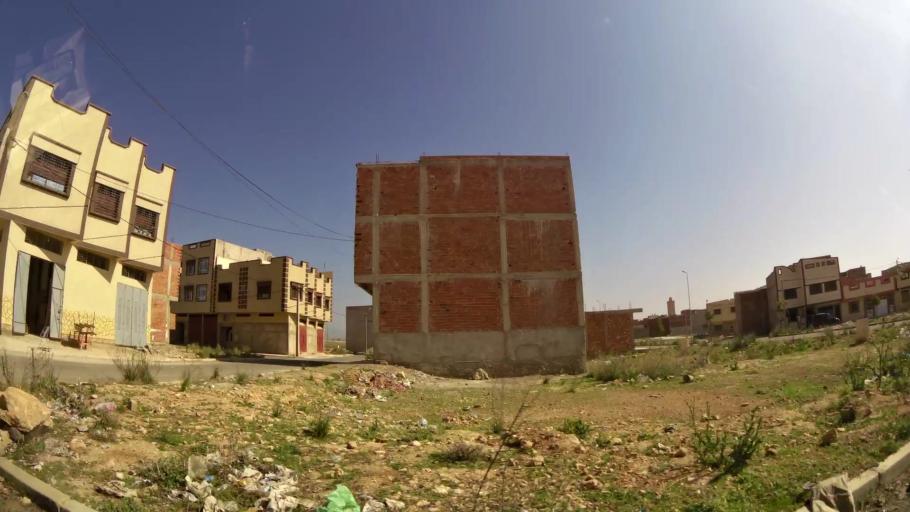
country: MA
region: Oriental
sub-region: Oujda-Angad
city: Oujda
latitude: 34.6969
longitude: -1.8701
